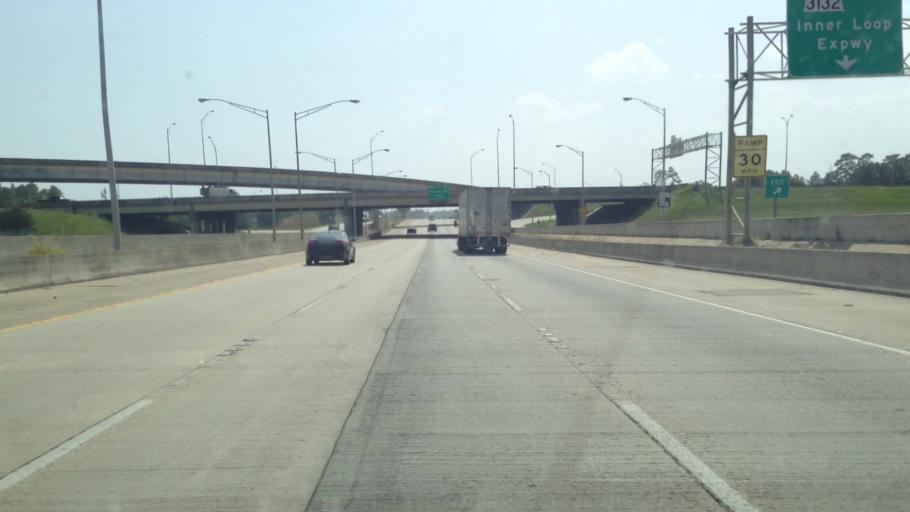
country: US
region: Louisiana
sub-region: Caddo Parish
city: Shreveport
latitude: 32.4569
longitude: -93.8428
